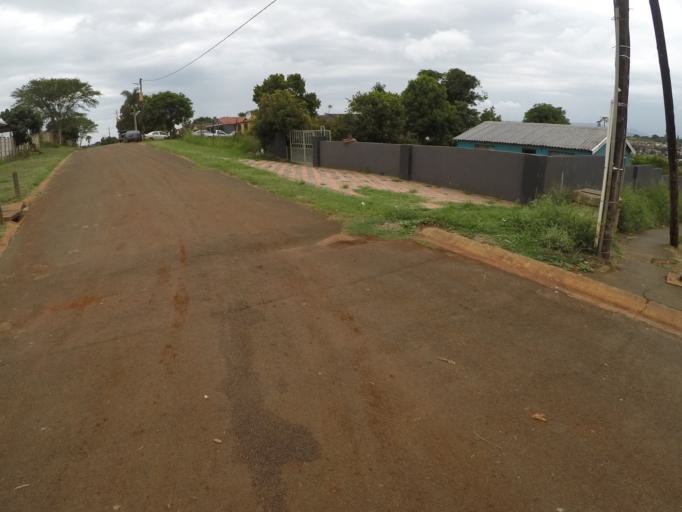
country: ZA
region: KwaZulu-Natal
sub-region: uThungulu District Municipality
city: Empangeni
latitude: -28.7748
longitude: 31.8613
